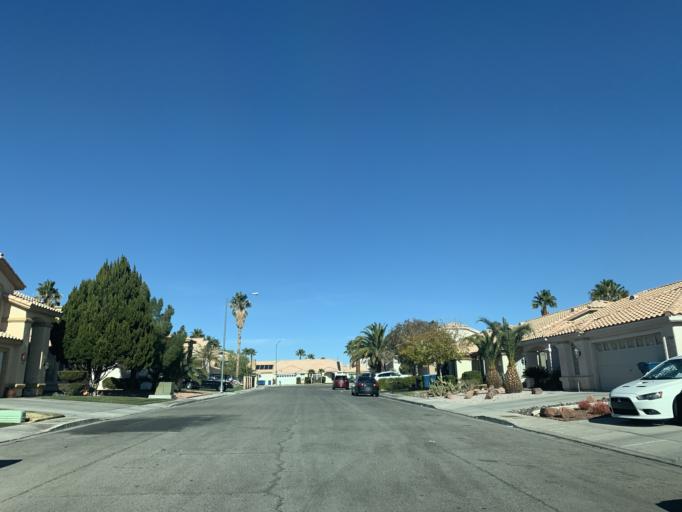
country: US
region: Nevada
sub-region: Clark County
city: Summerlin South
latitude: 36.1169
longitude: -115.2886
